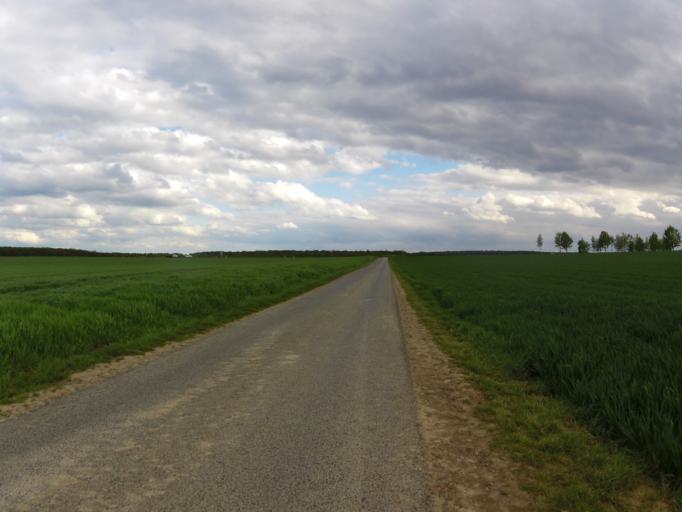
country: DE
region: Bavaria
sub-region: Regierungsbezirk Unterfranken
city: Unterpleichfeld
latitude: 49.8543
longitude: 10.0572
